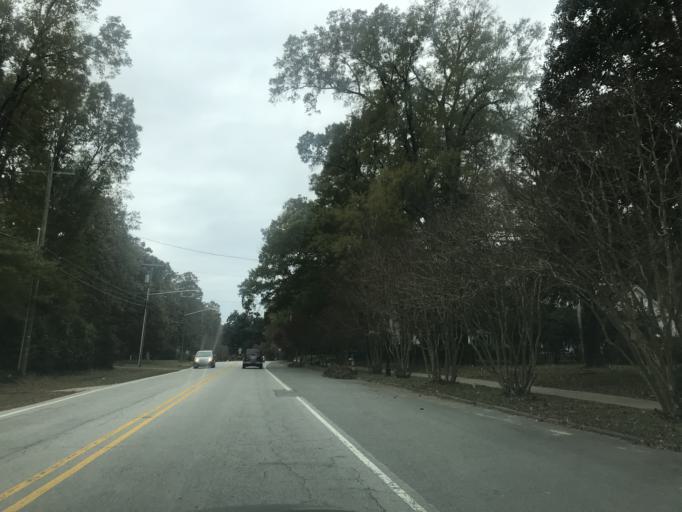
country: US
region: North Carolina
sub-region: Wake County
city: Wake Forest
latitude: 35.9890
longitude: -78.5055
